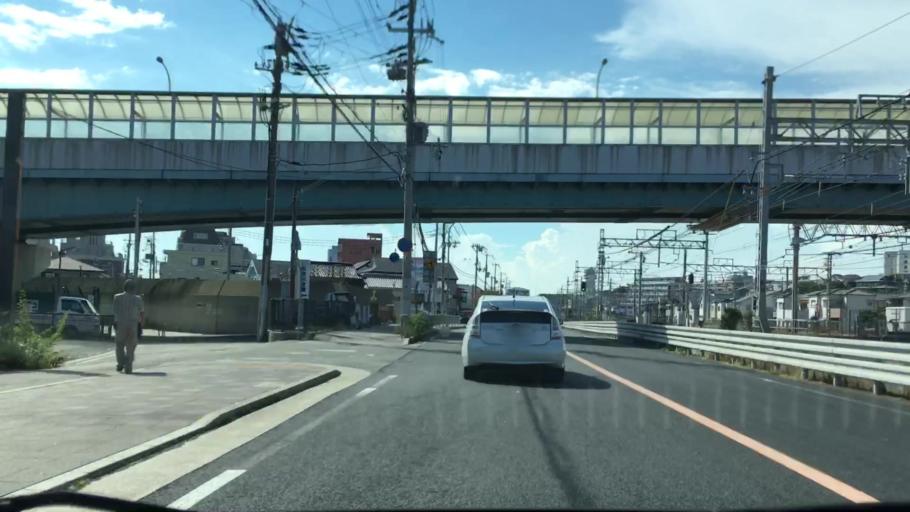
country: JP
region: Hyogo
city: Akashi
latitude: 34.6451
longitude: 135.0124
